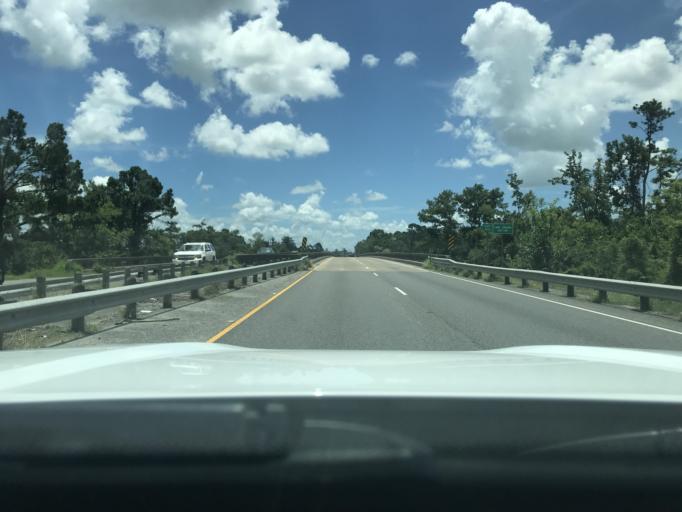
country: US
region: Louisiana
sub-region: Calcasieu Parish
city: Moss Bluff
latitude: 30.2736
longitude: -93.1827
